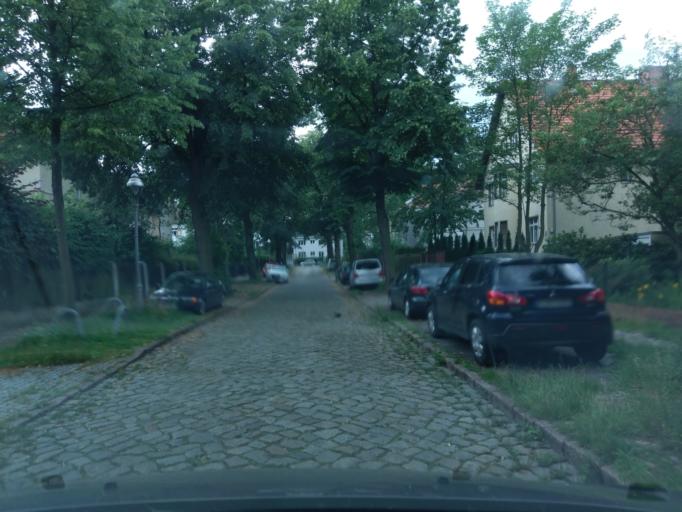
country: DE
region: Berlin
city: Lichterfelde
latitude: 52.4384
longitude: 13.3127
